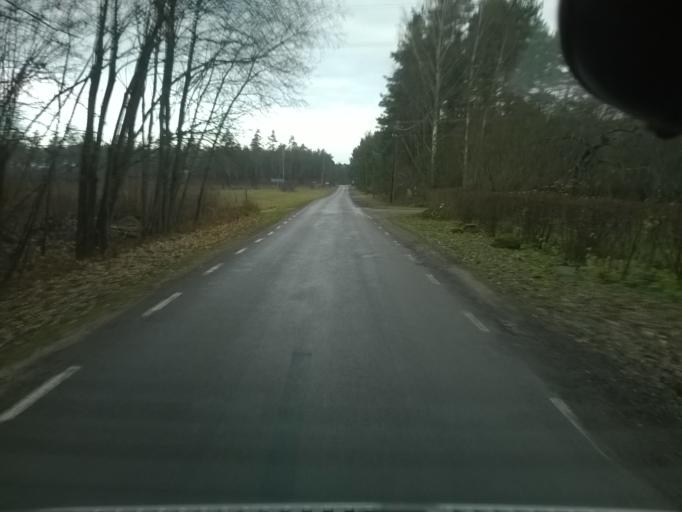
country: EE
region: Laeaene
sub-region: Ridala Parish
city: Uuemoisa
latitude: 58.9525
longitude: 23.7252
